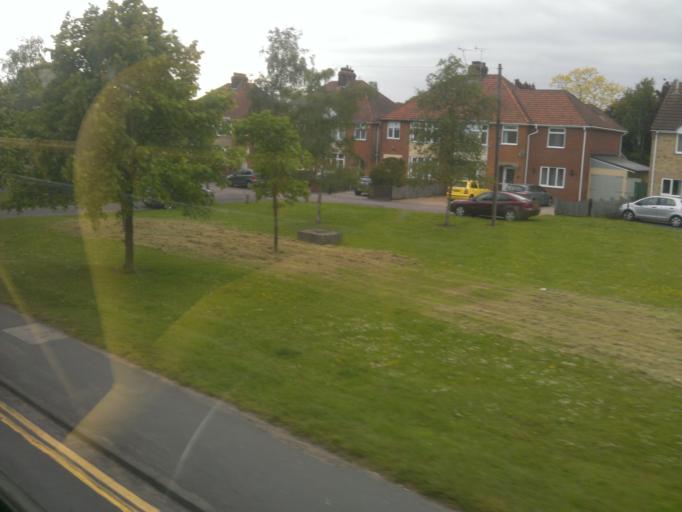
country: GB
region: England
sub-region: Essex
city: Colchester
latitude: 51.9110
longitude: 0.9276
